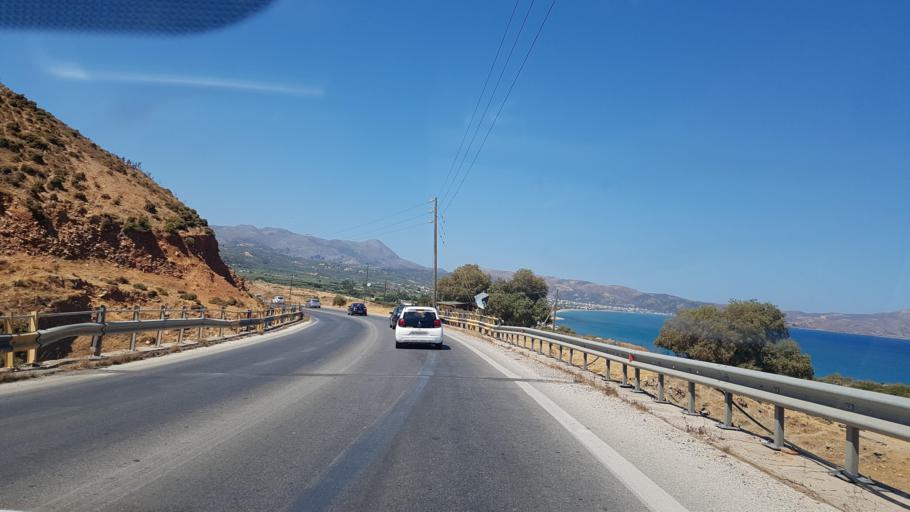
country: GR
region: Crete
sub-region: Nomos Chanias
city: Kolympari
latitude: 35.5081
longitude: 23.7227
